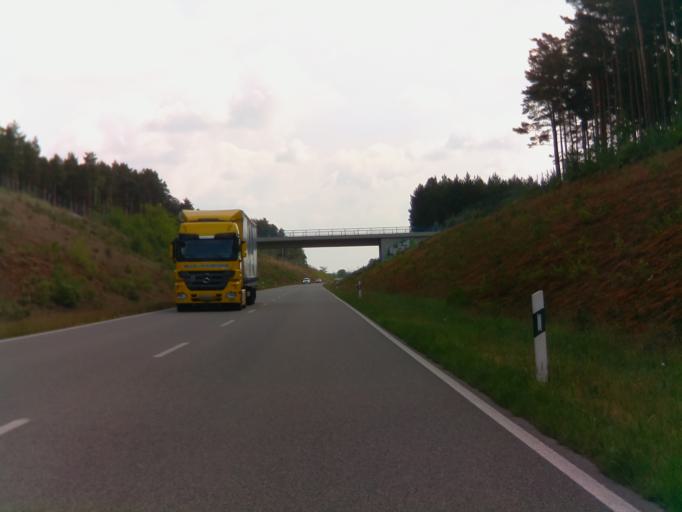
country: DE
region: Saxony-Anhalt
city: Uchtspringe
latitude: 52.5476
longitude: 11.6005
